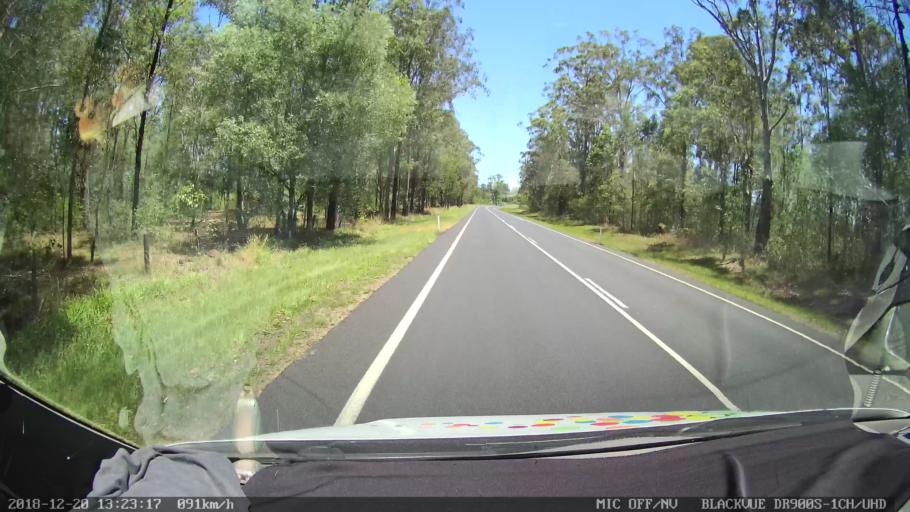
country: AU
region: New South Wales
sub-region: Richmond Valley
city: Casino
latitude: -29.1026
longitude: 153.0003
